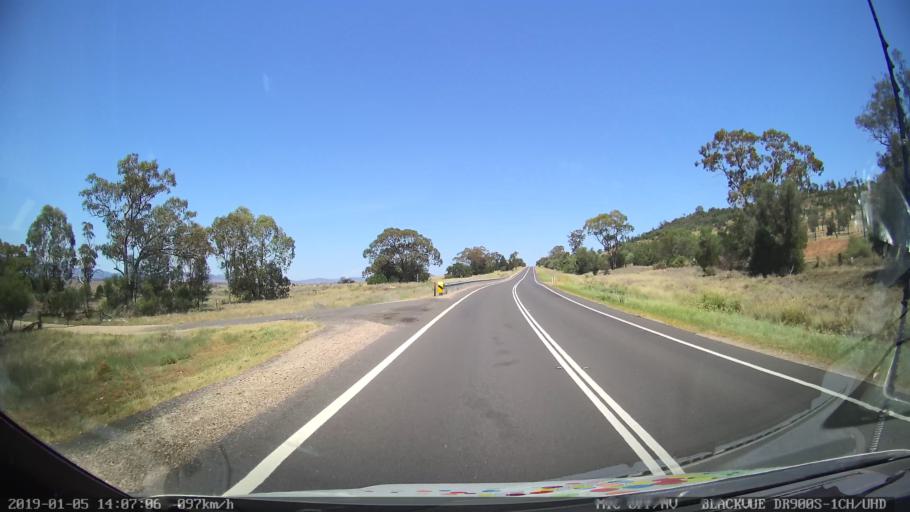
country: AU
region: New South Wales
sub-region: Gunnedah
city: Gunnedah
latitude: -31.2196
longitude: 150.4020
